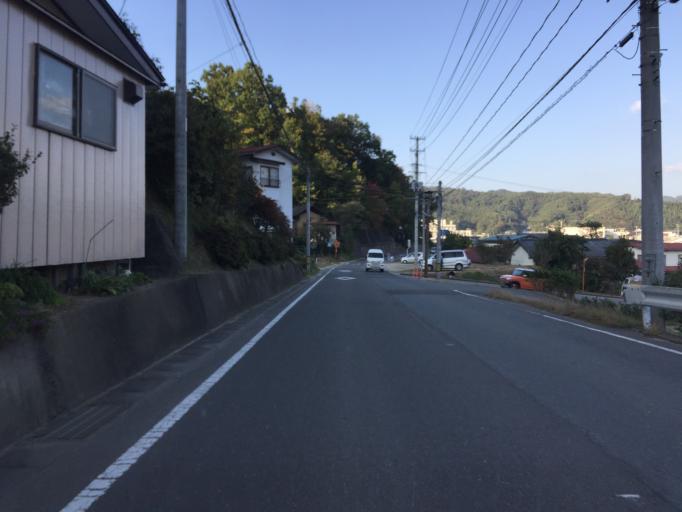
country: JP
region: Fukushima
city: Fukushima-shi
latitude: 37.6602
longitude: 140.5944
